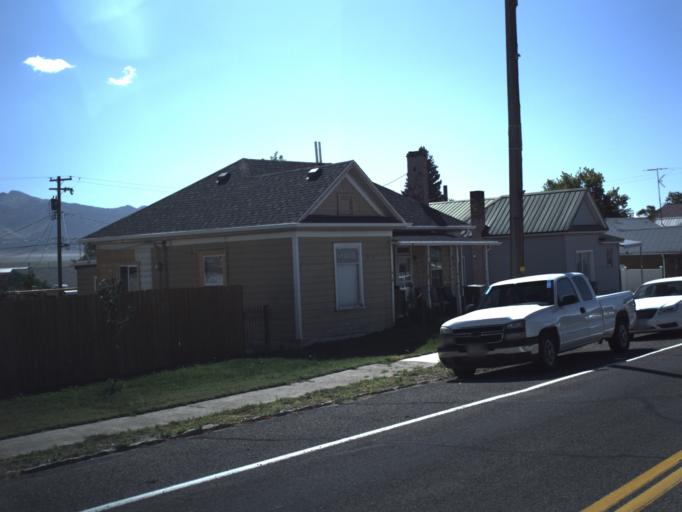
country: US
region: Utah
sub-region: Beaver County
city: Milford
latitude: 38.3998
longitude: -113.0102
